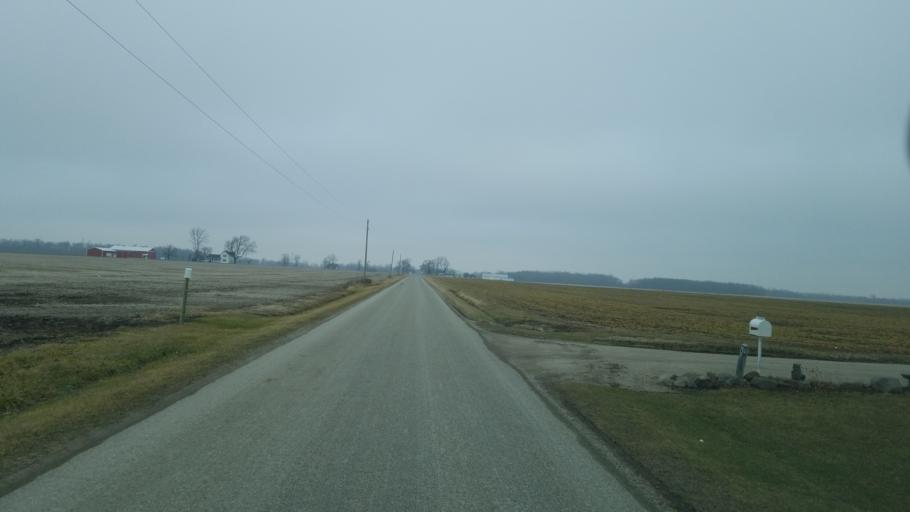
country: US
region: Indiana
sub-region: Adams County
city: Berne
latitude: 40.6846
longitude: -84.8549
